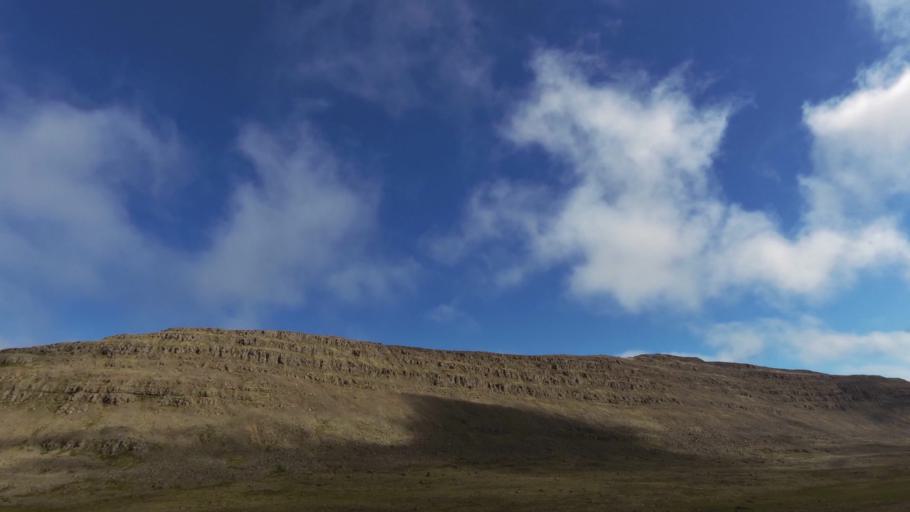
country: IS
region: West
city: Olafsvik
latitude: 65.5769
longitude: -24.0849
